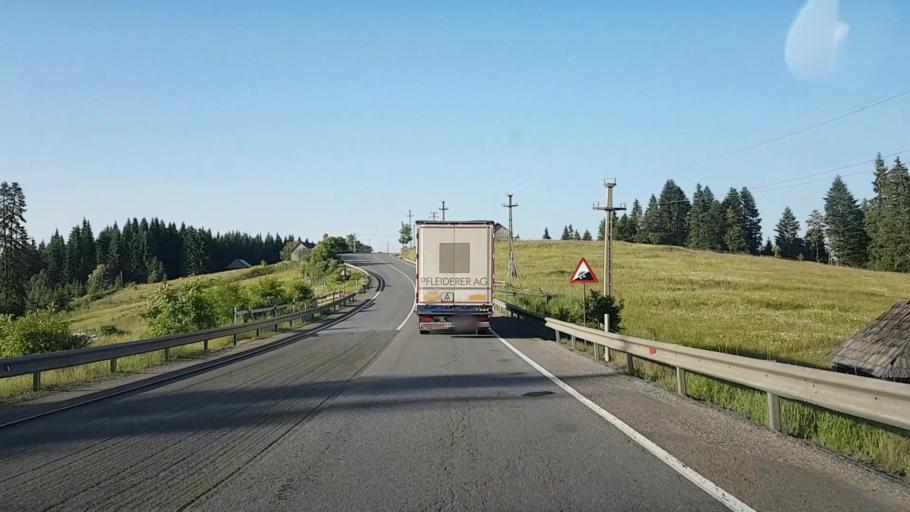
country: RO
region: Bistrita-Nasaud
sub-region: Comuna Lunca Ilvei
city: Lunca Ilvei
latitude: 47.2818
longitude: 25.0369
